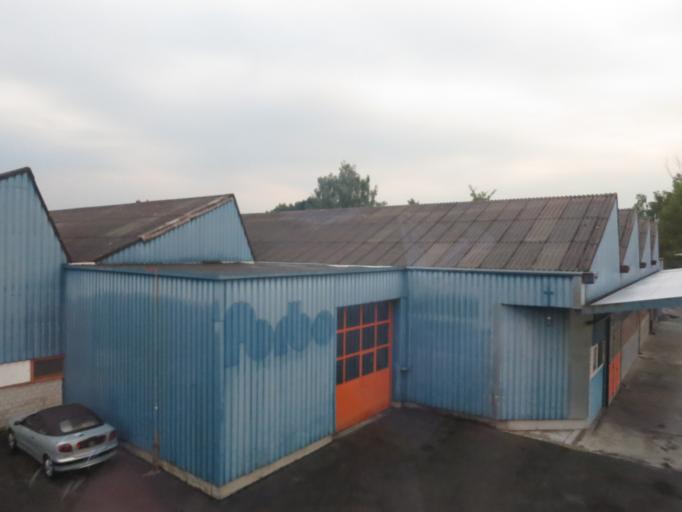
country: CH
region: Schwyz
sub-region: Bezirk March
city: Lachen
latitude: 47.1910
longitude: 8.8594
